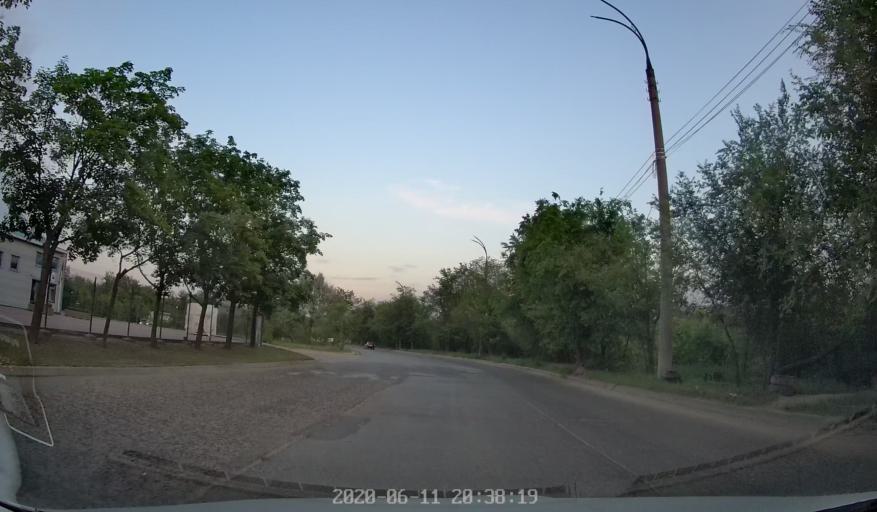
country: MD
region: Chisinau
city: Chisinau
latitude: 46.9989
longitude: 28.8832
